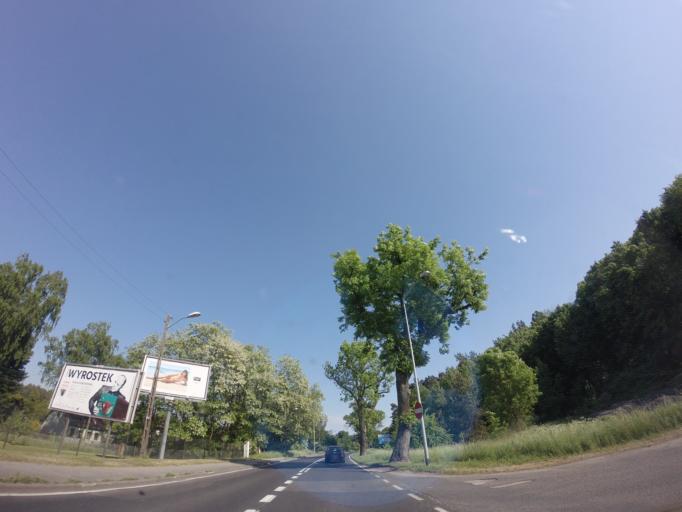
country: PL
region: West Pomeranian Voivodeship
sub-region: Powiat gryfinski
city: Stare Czarnowo
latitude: 53.3430
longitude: 14.7567
